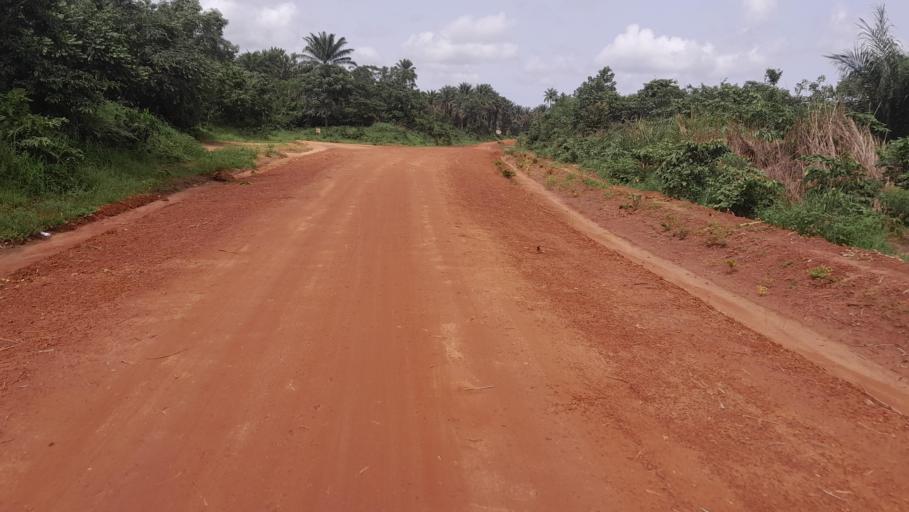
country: GN
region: Boke
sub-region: Boffa
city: Boffa
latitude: 10.0353
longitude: -13.8753
